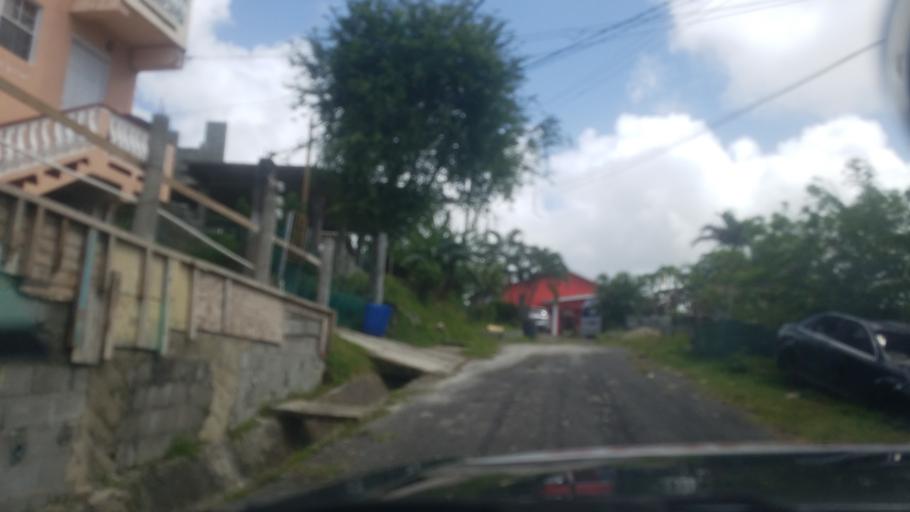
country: LC
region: Laborie Quarter
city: Laborie
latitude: 13.7424
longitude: -60.9701
